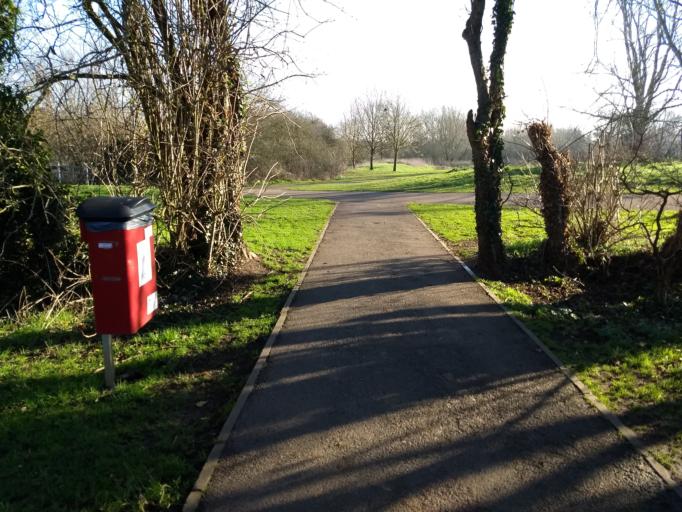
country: GB
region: England
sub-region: Buckinghamshire
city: Buckingham
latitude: 52.0017
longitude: -0.9801
